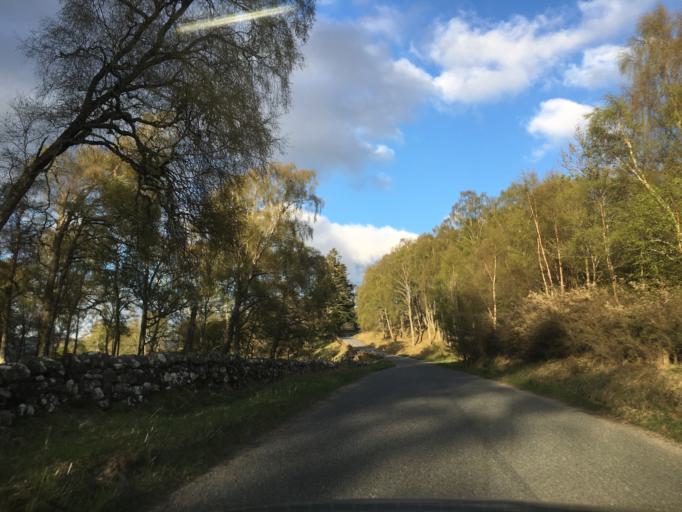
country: GB
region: Scotland
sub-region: Perth and Kinross
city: Aberfeldy
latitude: 56.6920
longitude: -3.9897
